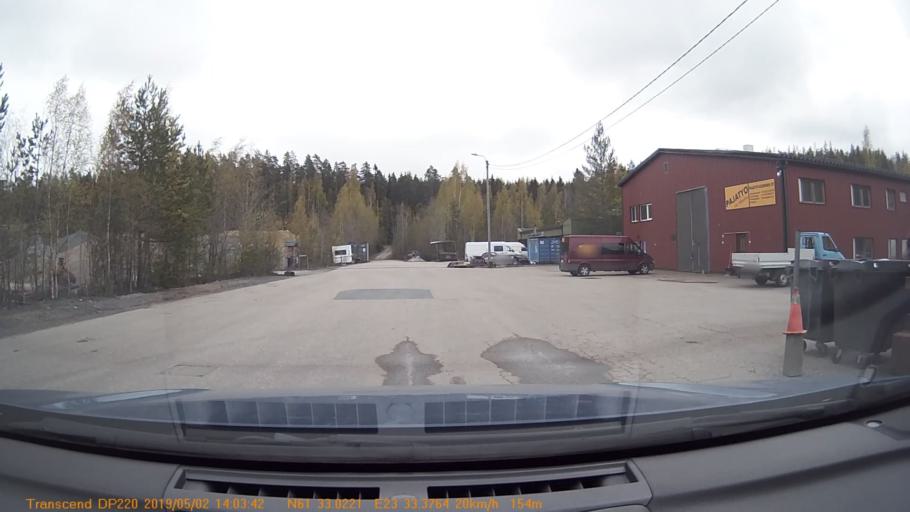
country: FI
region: Pirkanmaa
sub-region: Tampere
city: Yloejaervi
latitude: 61.5504
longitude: 23.5562
